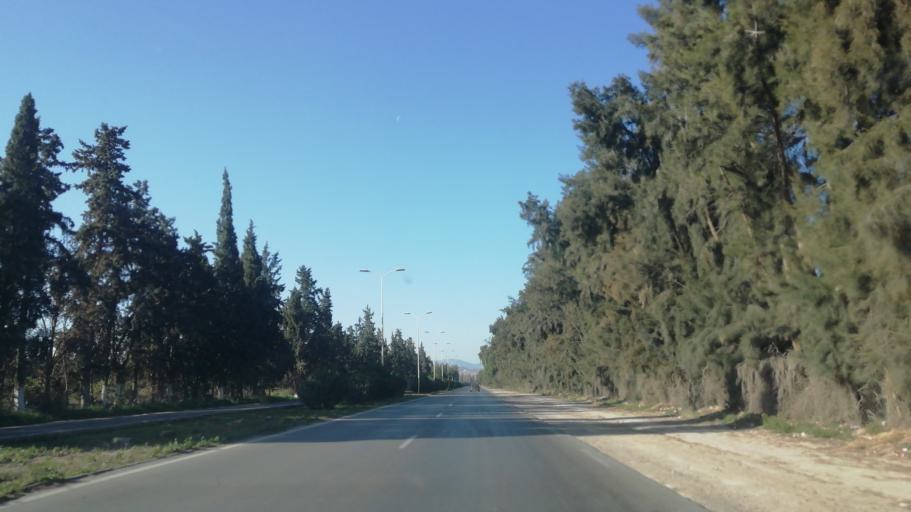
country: DZ
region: Mascara
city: Mascara
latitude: 35.6038
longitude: 0.0880
